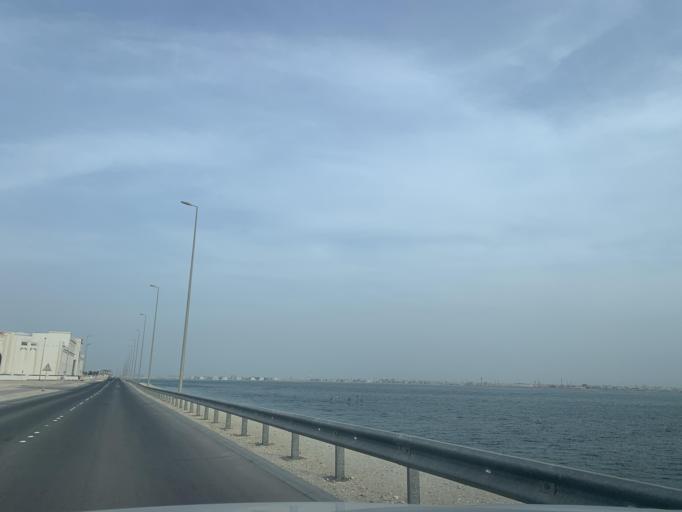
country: BH
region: Muharraq
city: Al Muharraq
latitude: 26.3082
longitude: 50.6187
